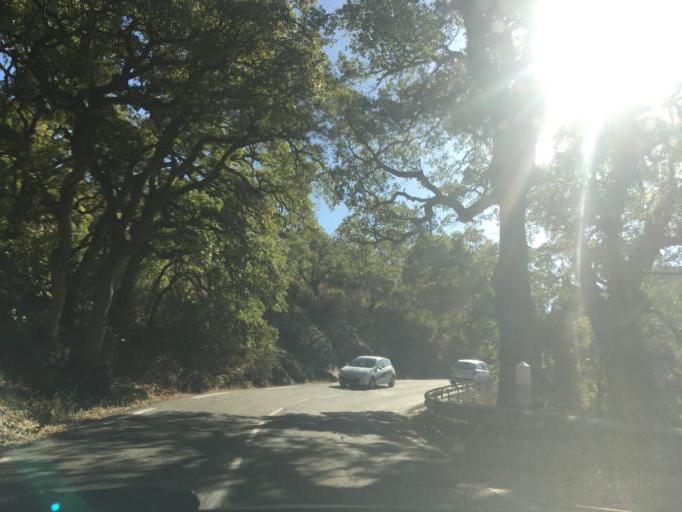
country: FR
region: Provence-Alpes-Cote d'Azur
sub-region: Departement du Var
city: La Garde-Freinet
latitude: 43.3311
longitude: 6.4573
